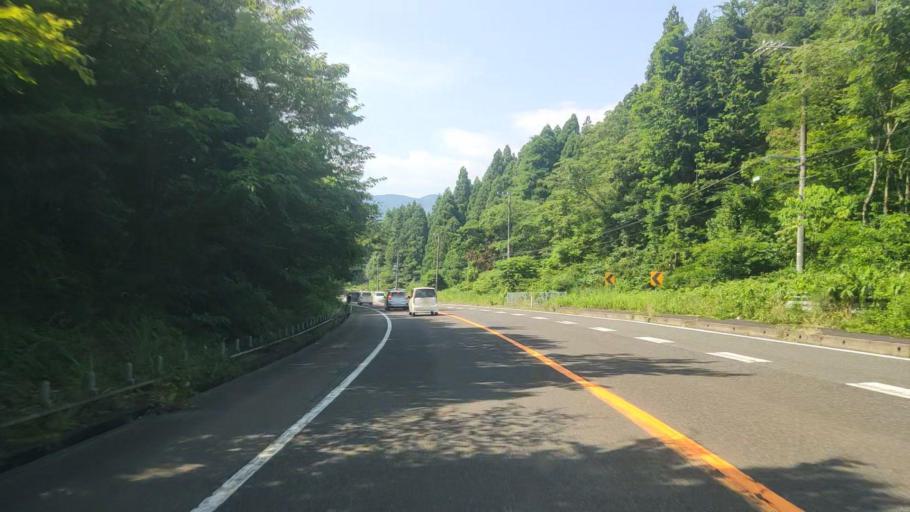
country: JP
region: Fukui
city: Tsuruga
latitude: 35.5933
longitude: 136.1236
